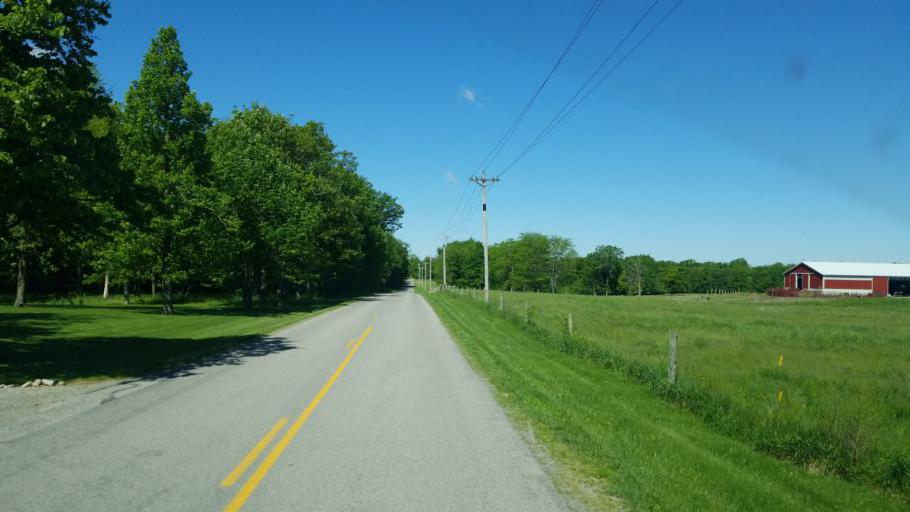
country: US
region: Ohio
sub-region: Logan County
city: Northwood
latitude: 40.4428
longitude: -83.6692
